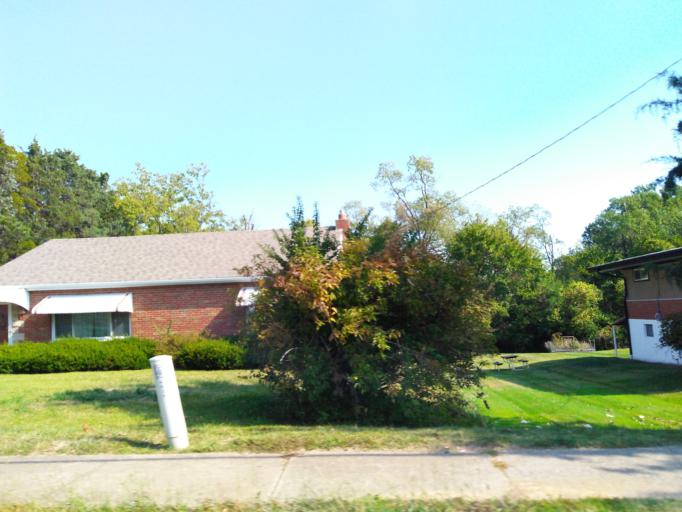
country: US
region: Missouri
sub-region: Saint Louis County
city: Concord
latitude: 38.5051
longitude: -90.3672
